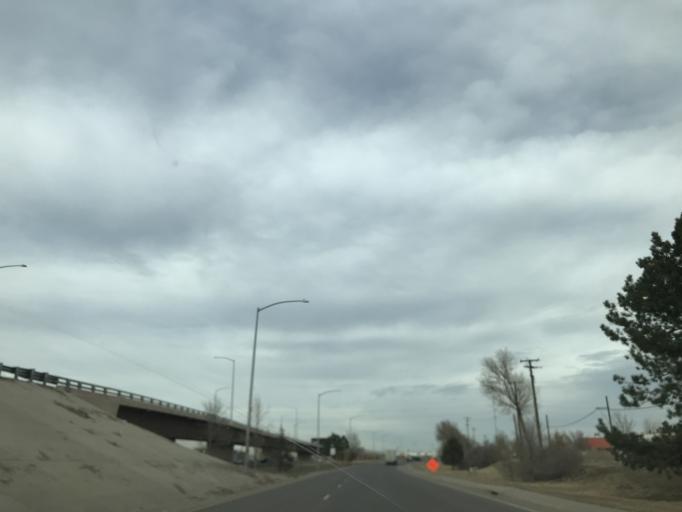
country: US
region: Colorado
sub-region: Adams County
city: Commerce City
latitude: 39.7920
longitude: -104.9395
